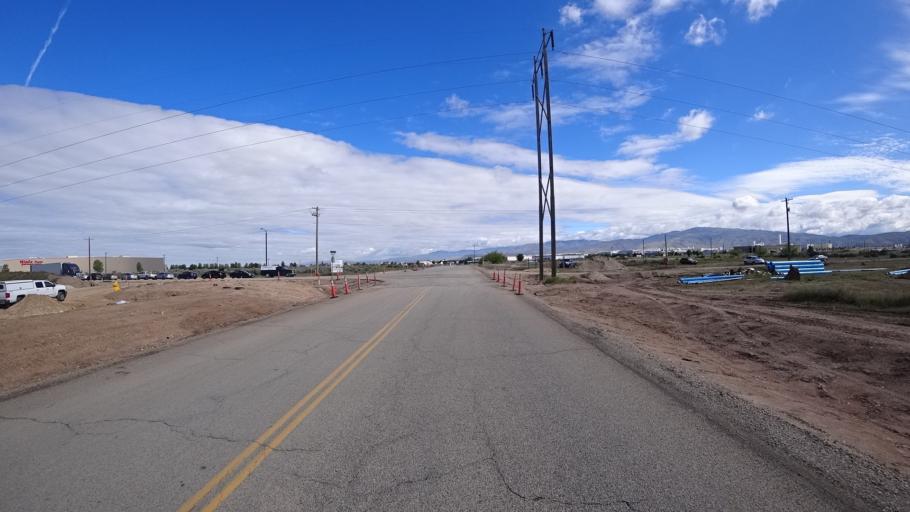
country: US
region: Idaho
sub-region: Ada County
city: Boise
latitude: 43.5161
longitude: -116.1514
